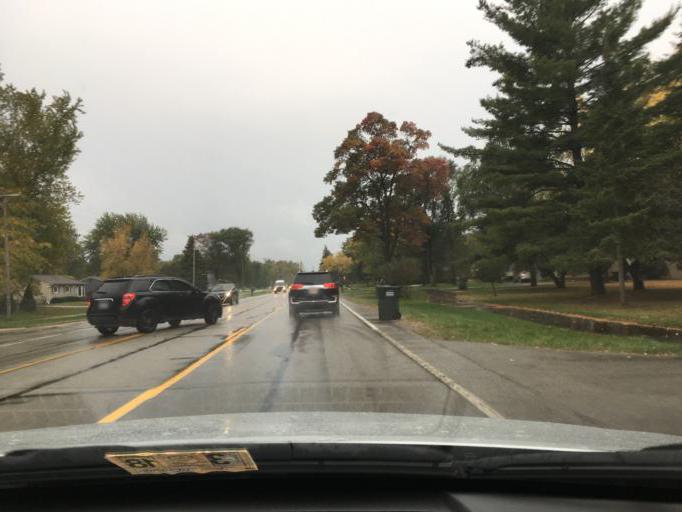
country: US
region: Michigan
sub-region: Oakland County
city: Rochester Hills
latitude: 42.6347
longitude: -83.1117
